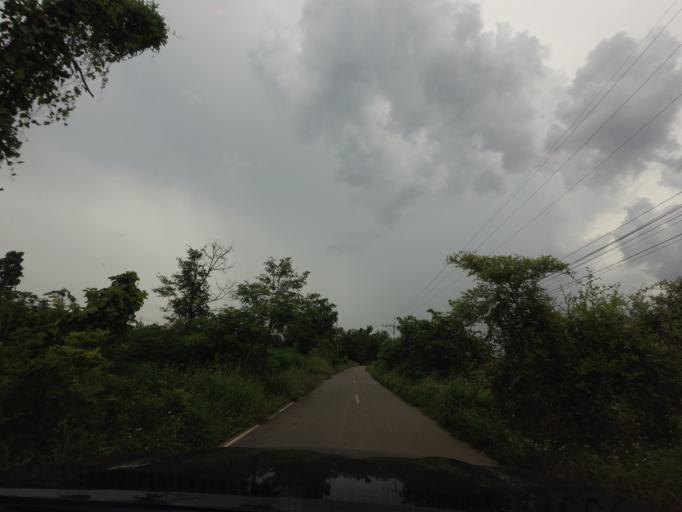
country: TH
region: Khon Kaen
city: Wiang Kao
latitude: 16.6798
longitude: 102.2710
